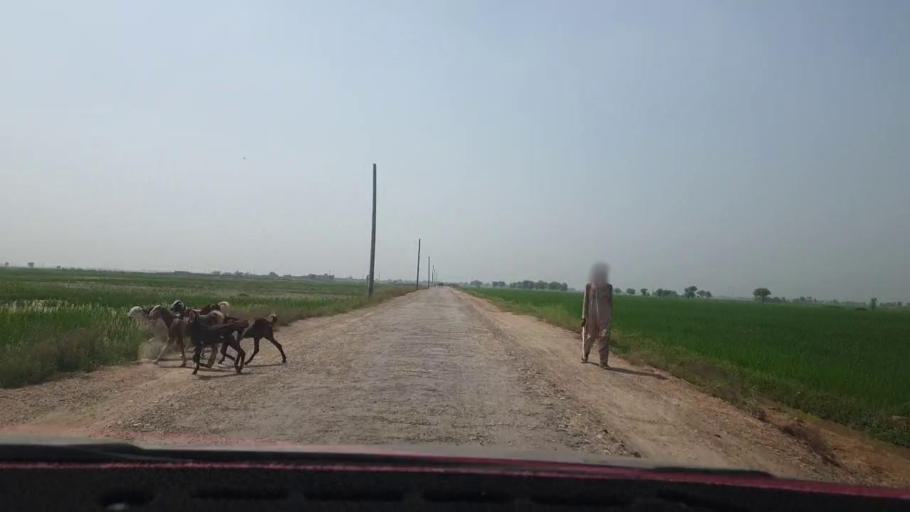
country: PK
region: Sindh
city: Warah
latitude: 27.4112
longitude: 67.8446
